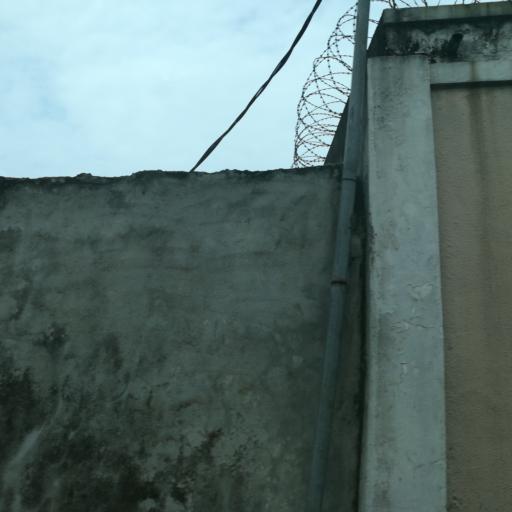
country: NG
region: Rivers
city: Port Harcourt
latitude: 4.8223
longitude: 6.9849
